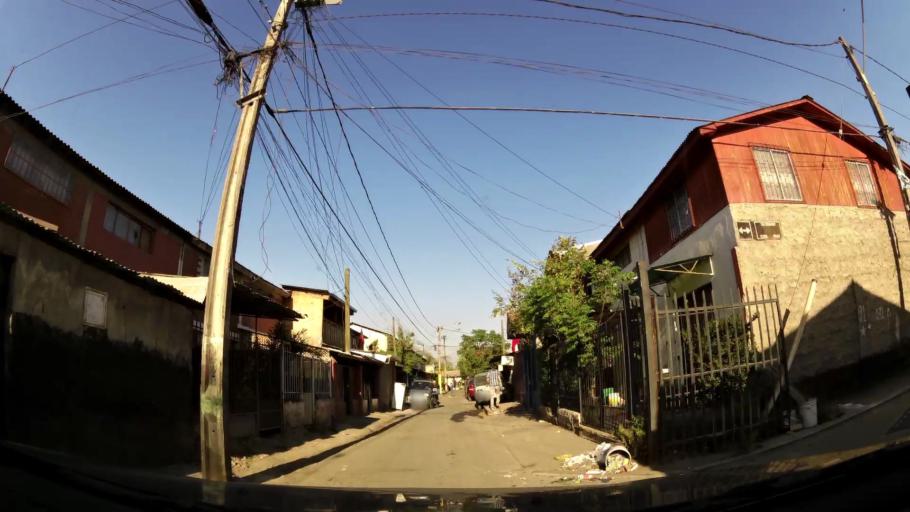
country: CL
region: Santiago Metropolitan
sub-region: Provincia de Santiago
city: La Pintana
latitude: -33.5789
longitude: -70.6625
